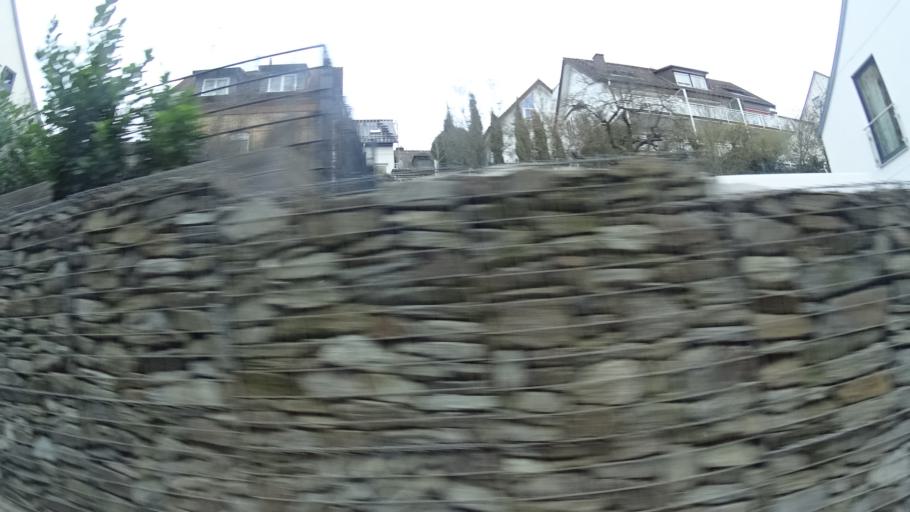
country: DE
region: Hesse
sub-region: Regierungsbezirk Darmstadt
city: Wiesbaden
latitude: 50.1147
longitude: 8.2734
